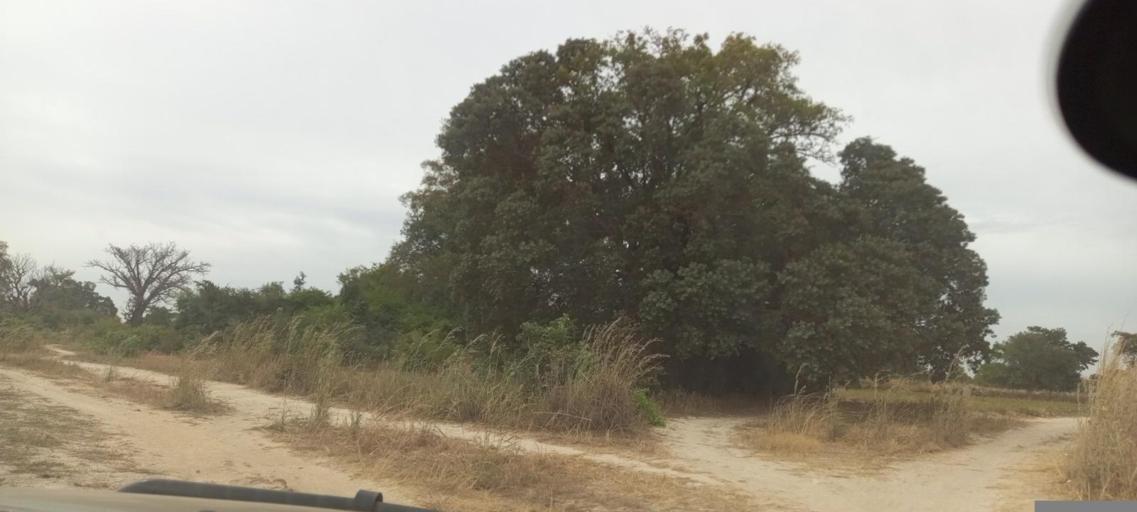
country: ML
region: Koulikoro
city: Kati
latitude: 12.7522
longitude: -8.3120
